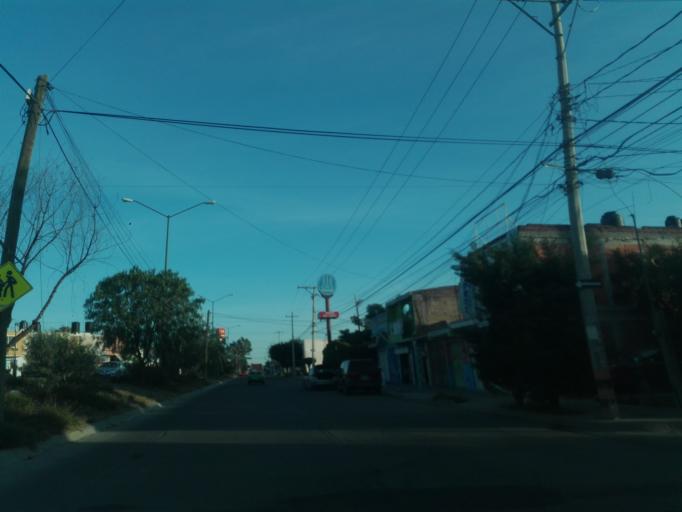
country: MX
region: Guanajuato
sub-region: Leon
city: San Jose de Duran (Los Troncoso)
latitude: 21.0851
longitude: -101.6449
